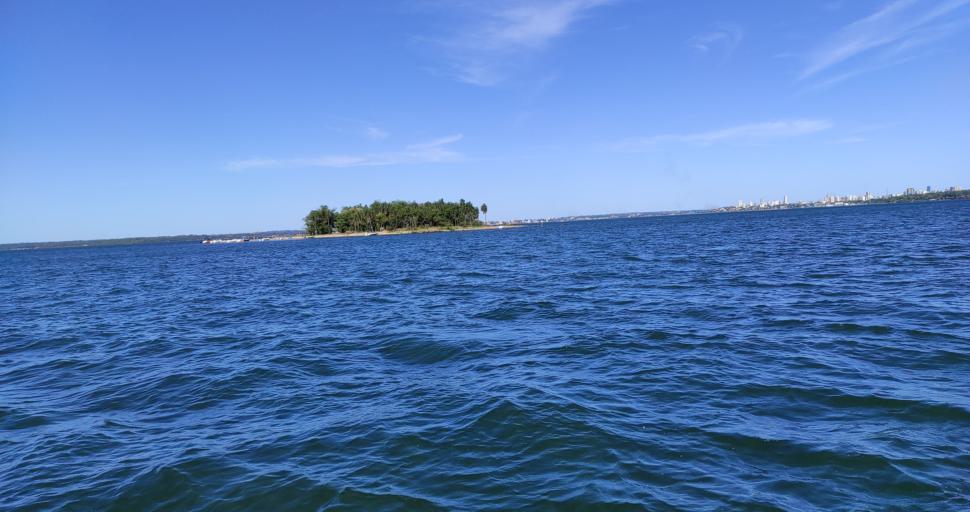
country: PY
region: Itapua
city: San Juan del Parana
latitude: -27.3409
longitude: -55.9538
